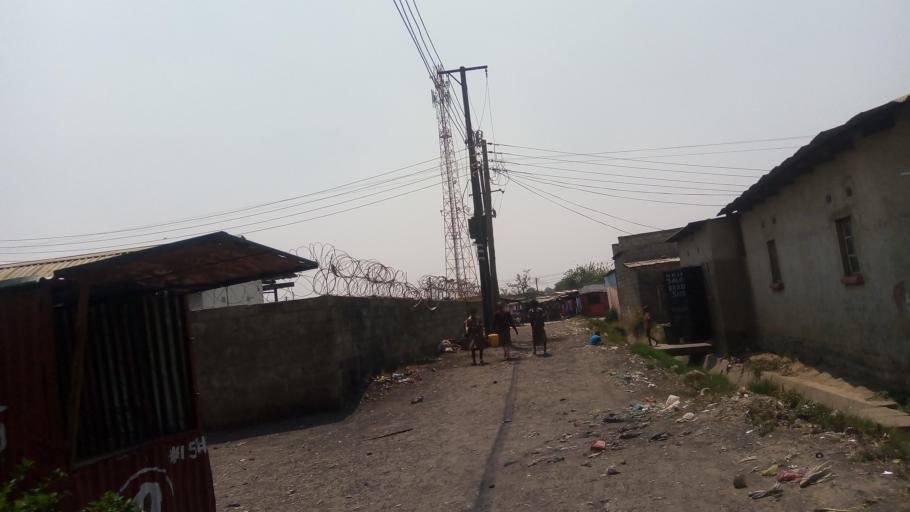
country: ZM
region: Lusaka
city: Lusaka
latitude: -15.4437
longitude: 28.3799
